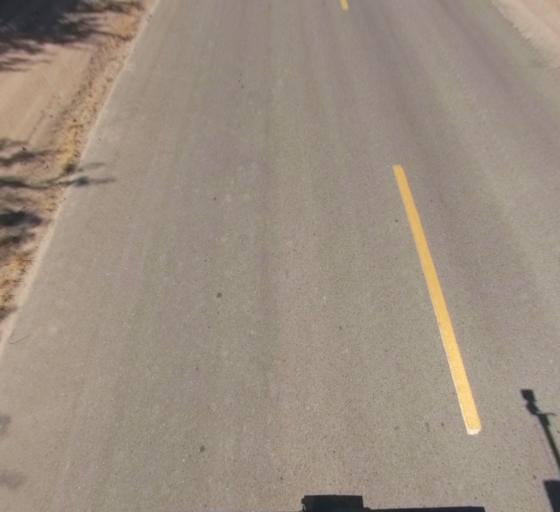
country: US
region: California
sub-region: Fresno County
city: Biola
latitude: 36.8689
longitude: -119.9470
